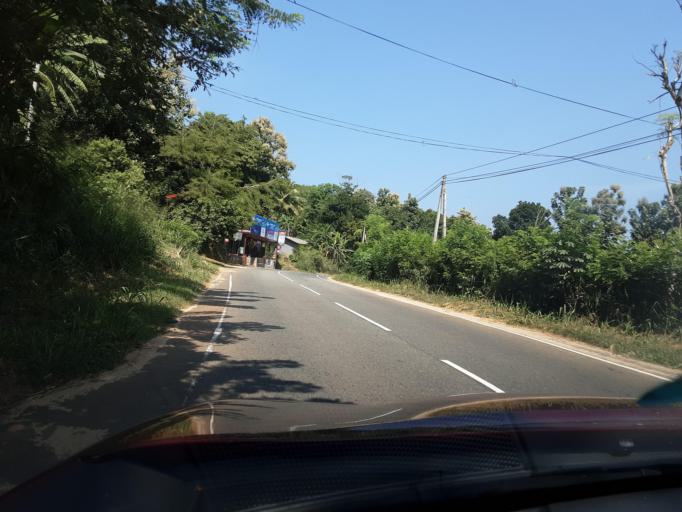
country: LK
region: Uva
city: Badulla
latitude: 7.1772
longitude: 81.0486
